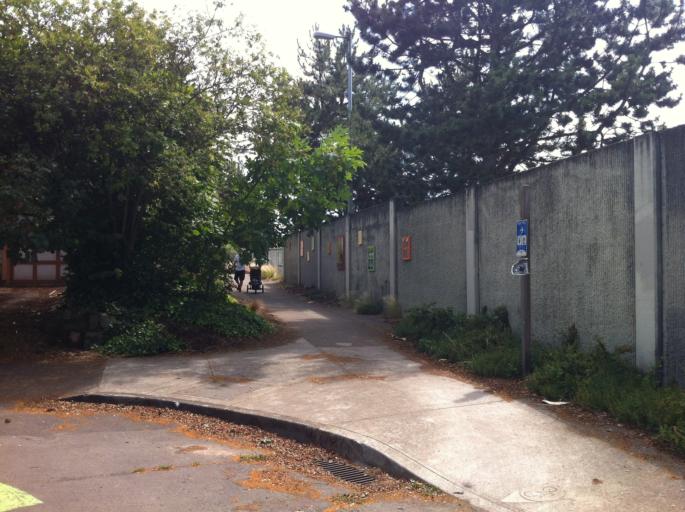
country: US
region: Oregon
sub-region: Multnomah County
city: Portland
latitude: 45.5736
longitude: -122.6781
